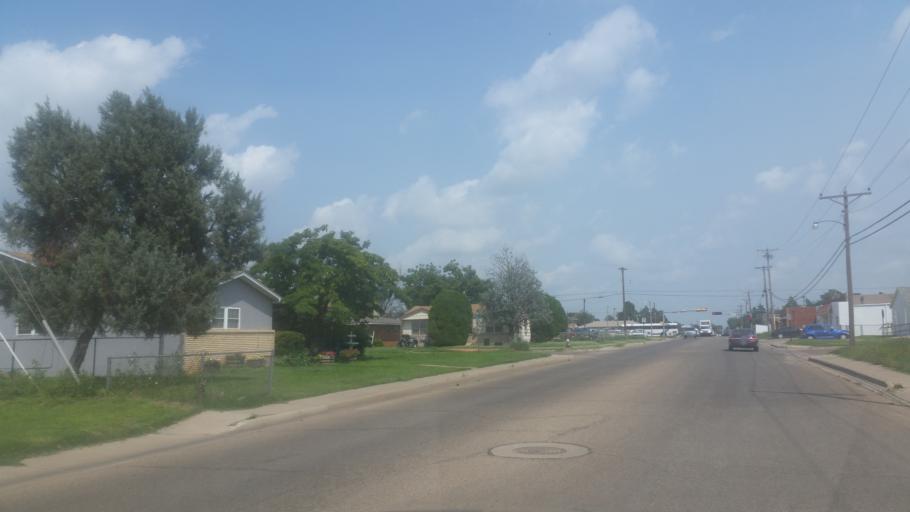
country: US
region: New Mexico
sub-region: Curry County
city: Clovis
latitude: 34.4120
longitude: -103.2160
